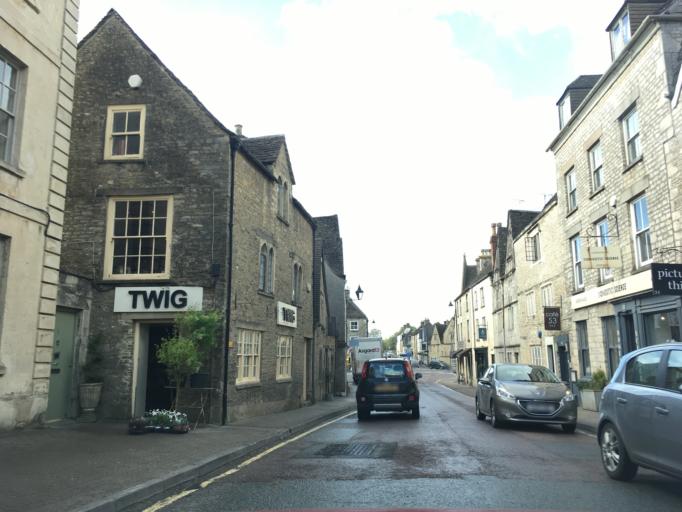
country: GB
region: England
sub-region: Gloucestershire
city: Tetbury
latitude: 51.6384
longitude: -2.1615
